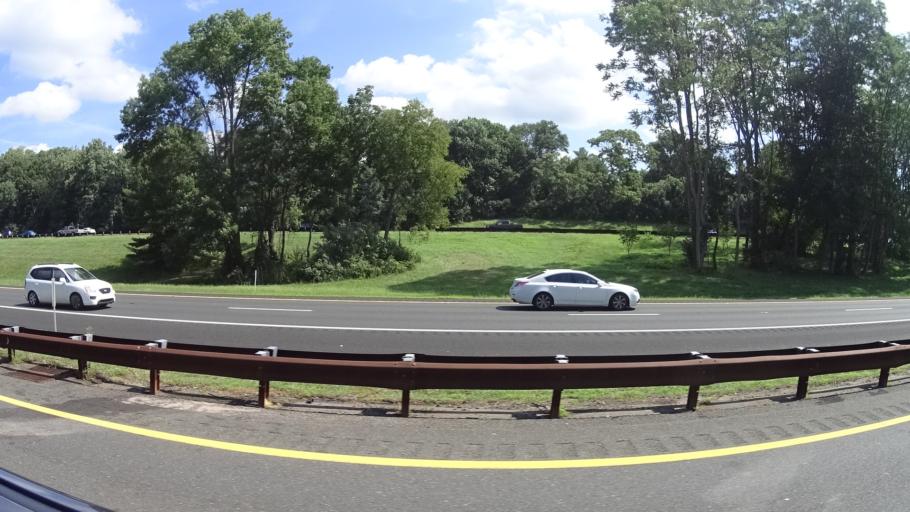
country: US
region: New Jersey
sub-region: Monmouth County
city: Lincroft
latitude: 40.3658
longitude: -74.1416
